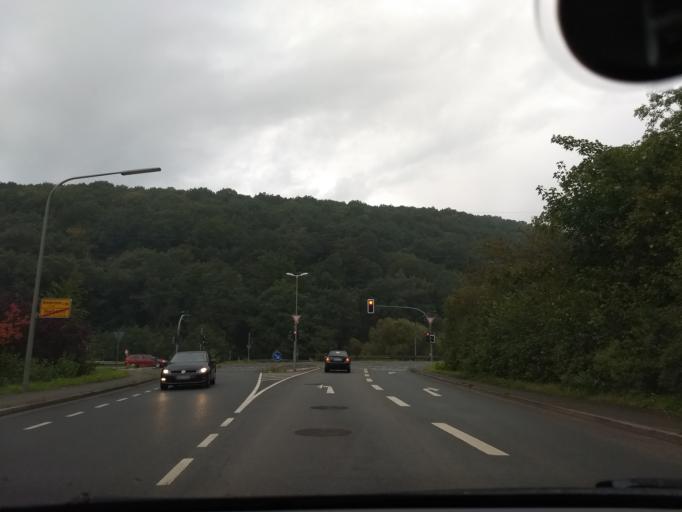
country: DE
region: North Rhine-Westphalia
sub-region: Regierungsbezirk Arnsberg
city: Werl
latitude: 51.4585
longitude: 7.9725
